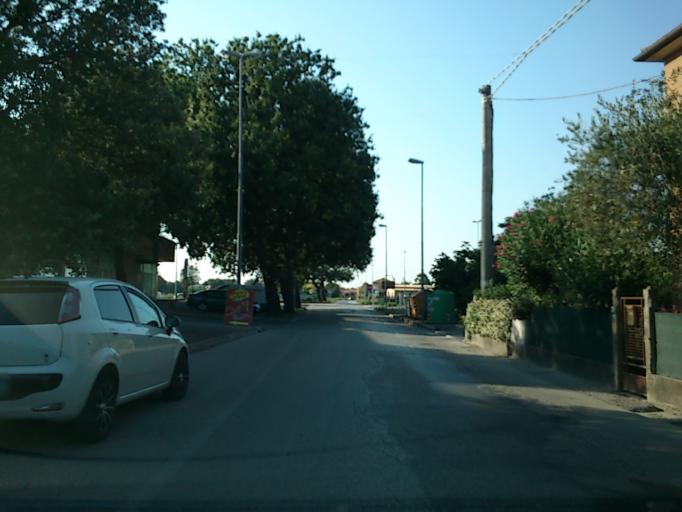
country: IT
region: The Marches
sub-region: Provincia di Pesaro e Urbino
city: Fano
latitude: 43.8283
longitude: 13.0413
